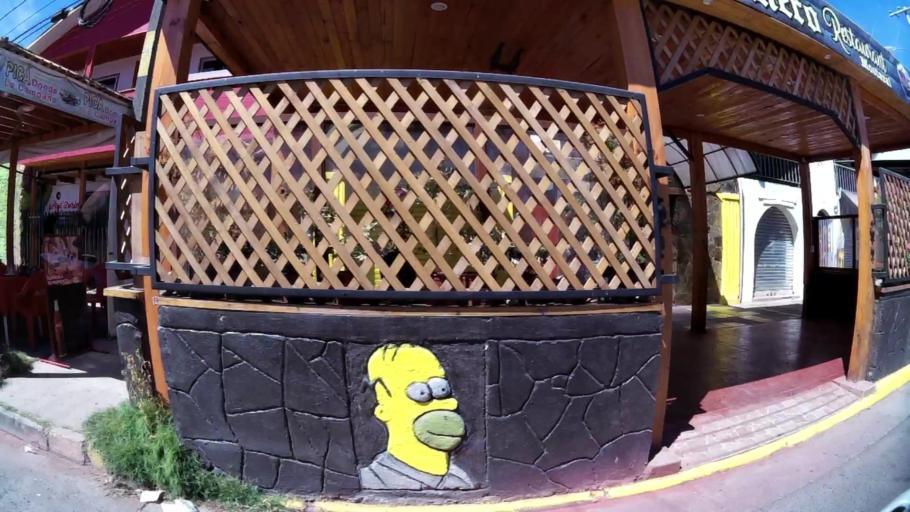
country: CL
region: O'Higgins
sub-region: Provincia de Cachapoal
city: Graneros
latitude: -33.9772
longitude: -70.7127
